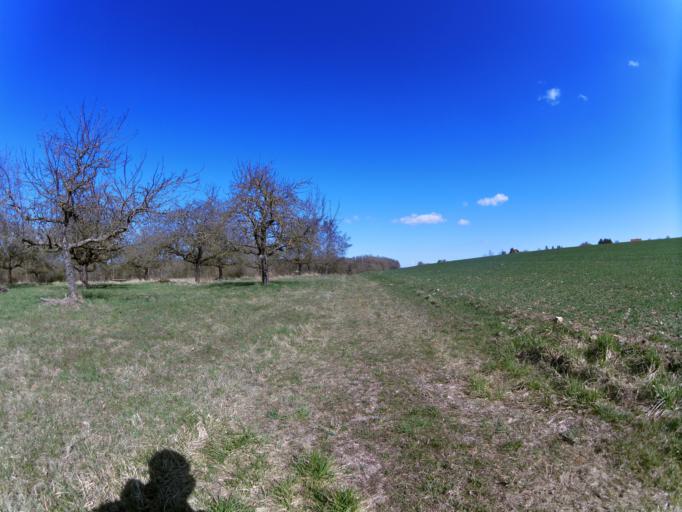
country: DE
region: Bavaria
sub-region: Regierungsbezirk Unterfranken
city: Hettstadt
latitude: 49.8020
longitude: 9.8024
